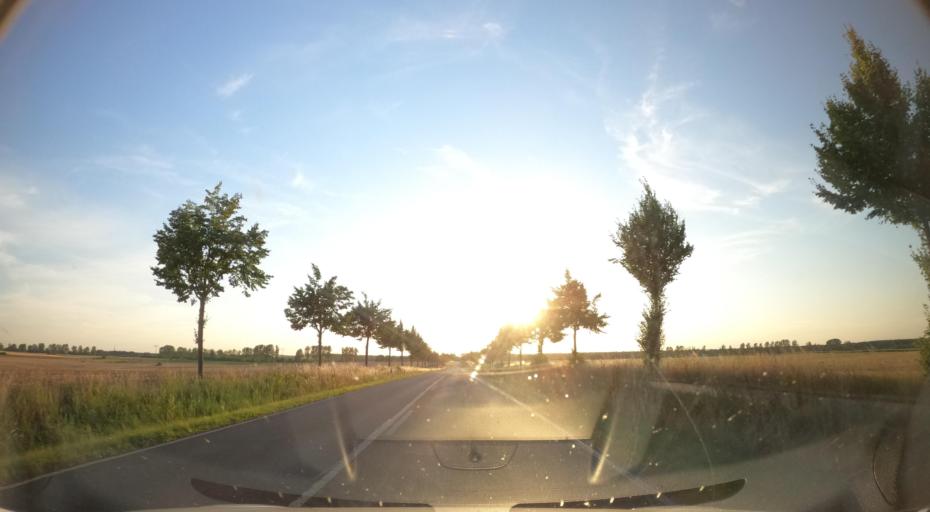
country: DE
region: Mecklenburg-Vorpommern
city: Viereck
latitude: 53.4979
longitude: 14.0739
